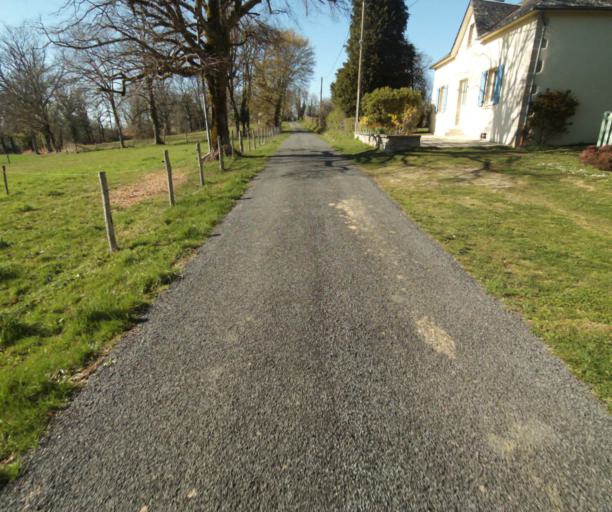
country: FR
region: Limousin
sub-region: Departement de la Correze
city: Chamboulive
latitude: 45.4041
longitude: 1.6618
